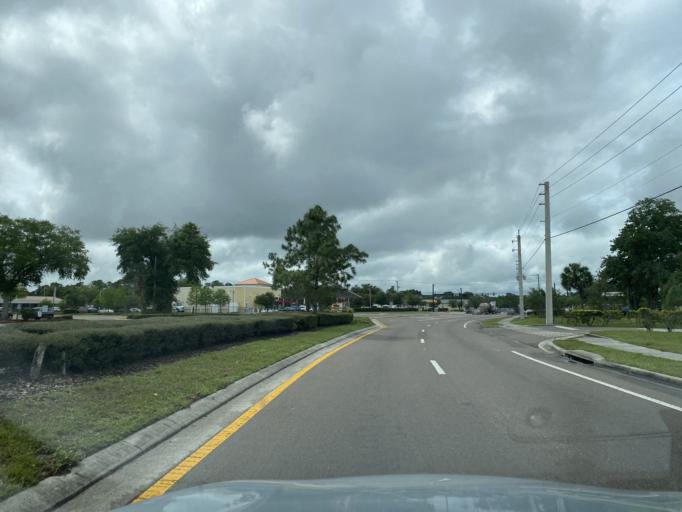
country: US
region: Florida
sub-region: Seminole County
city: Sanford
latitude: 28.7883
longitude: -81.2980
